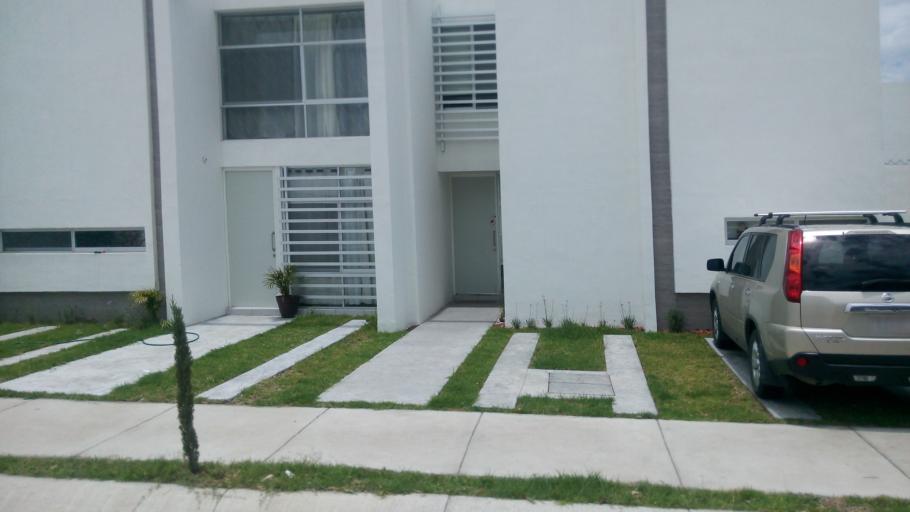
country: MX
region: Aguascalientes
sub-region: Aguascalientes
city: San Sebastian [Fraccionamiento]
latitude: 21.8302
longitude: -102.3183
